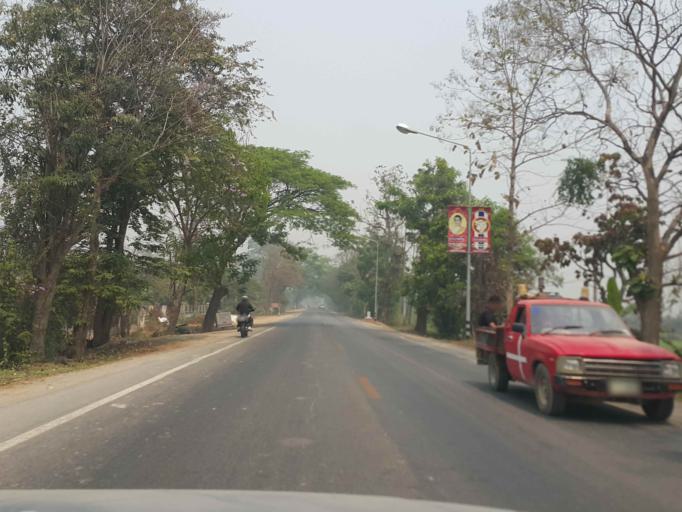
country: TH
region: Chiang Mai
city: Mae Taeng
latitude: 19.0064
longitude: 98.9718
